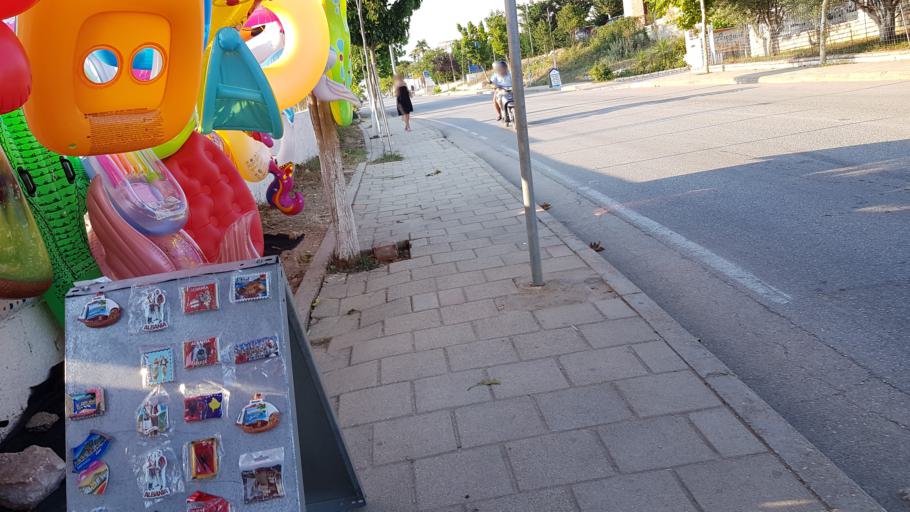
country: AL
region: Vlore
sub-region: Rrethi i Sarandes
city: Xarre
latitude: 39.7702
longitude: 20.0038
